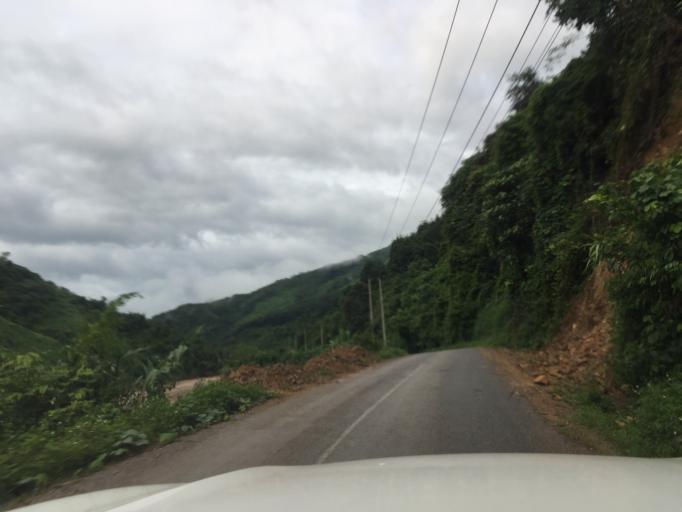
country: LA
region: Oudomxai
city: Muang La
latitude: 21.0263
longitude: 102.2350
